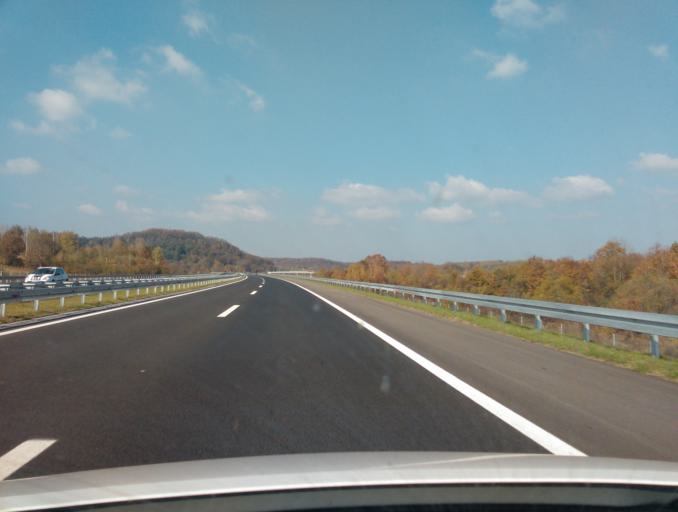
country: BA
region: Republika Srpska
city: Prnjavor
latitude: 44.8847
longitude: 17.6169
